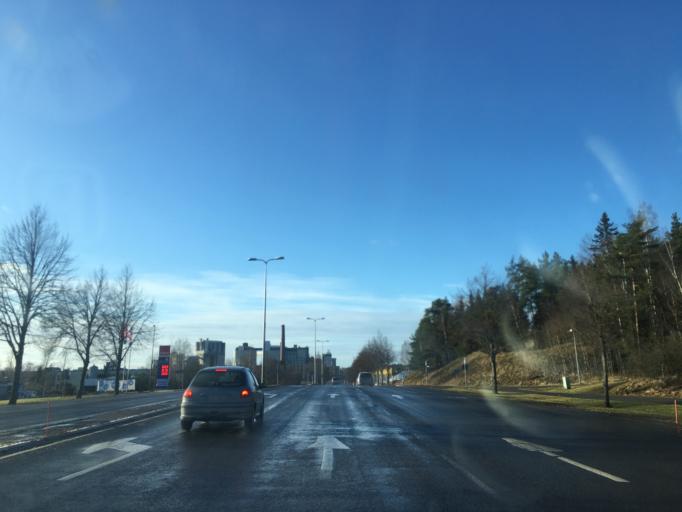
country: FI
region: Varsinais-Suomi
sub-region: Turku
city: Raisio
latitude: 60.4863
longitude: 22.1500
